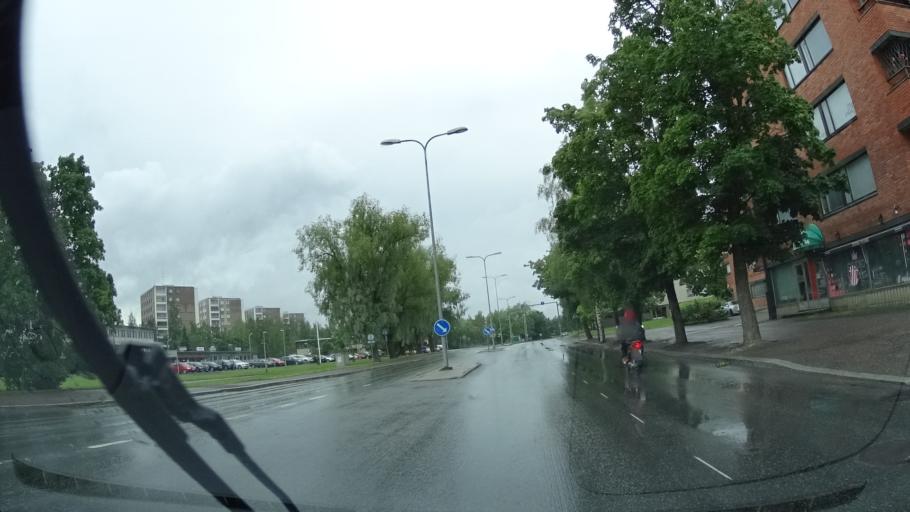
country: FI
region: Haeme
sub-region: Forssa
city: Forssa
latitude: 60.8112
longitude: 23.6155
